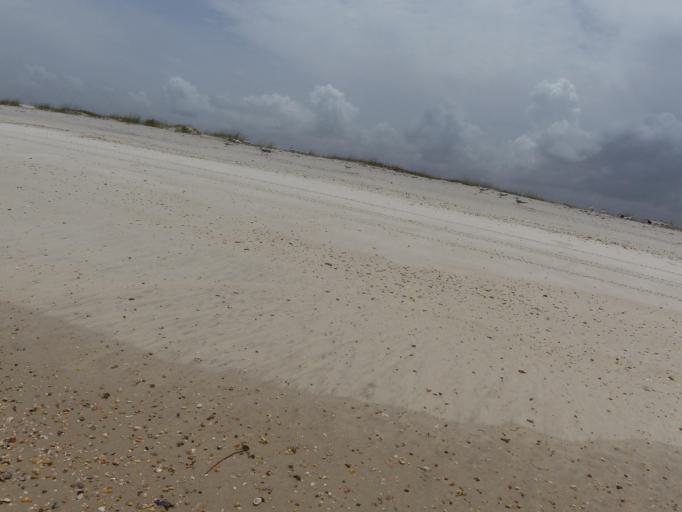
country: US
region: Florida
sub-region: Saint Johns County
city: Saint Augustine
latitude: 29.9019
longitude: -81.2771
